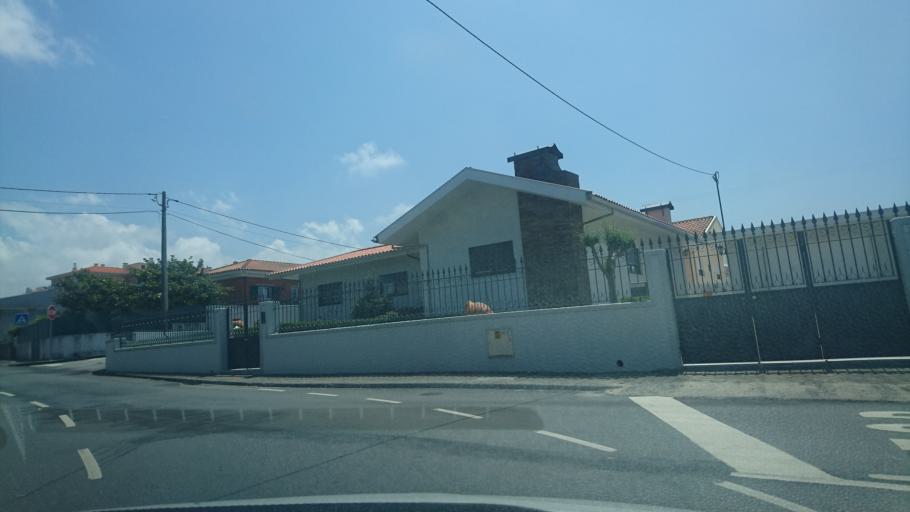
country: PT
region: Aveiro
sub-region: Ovar
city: Esmoriz
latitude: 40.9527
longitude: -8.6277
